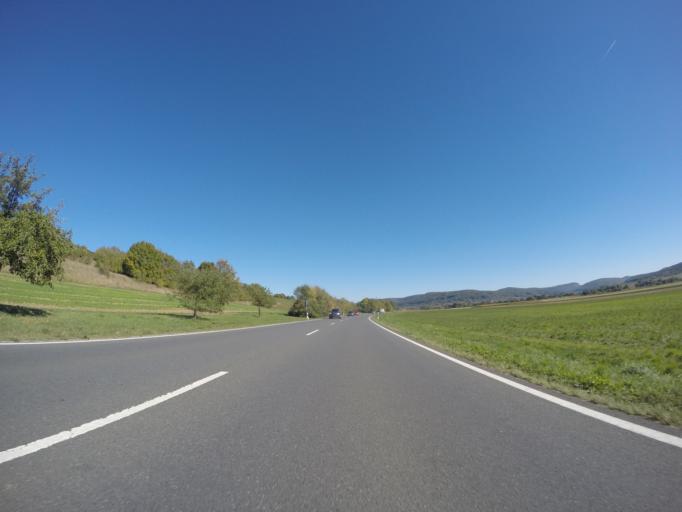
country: DE
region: Bavaria
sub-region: Upper Franconia
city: Kirchehrenbach
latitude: 49.7514
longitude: 11.1434
